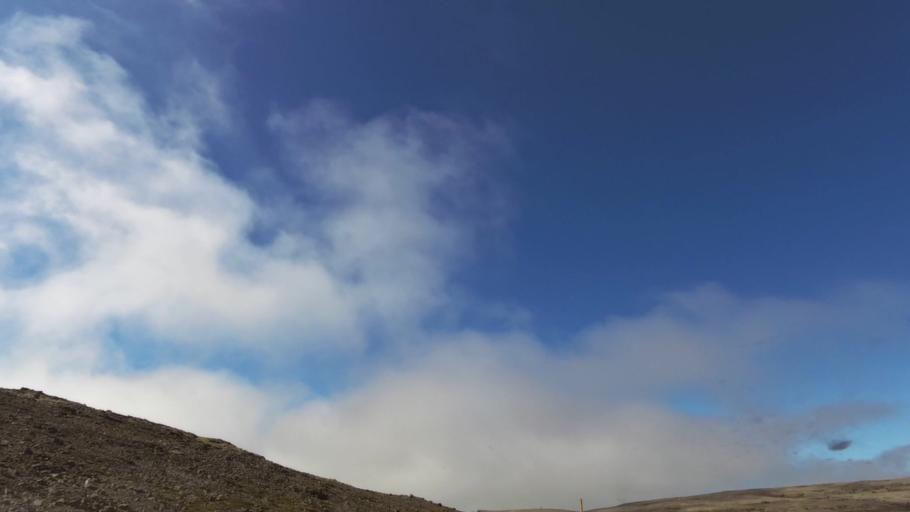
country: IS
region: West
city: Olafsvik
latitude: 65.5542
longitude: -24.2283
